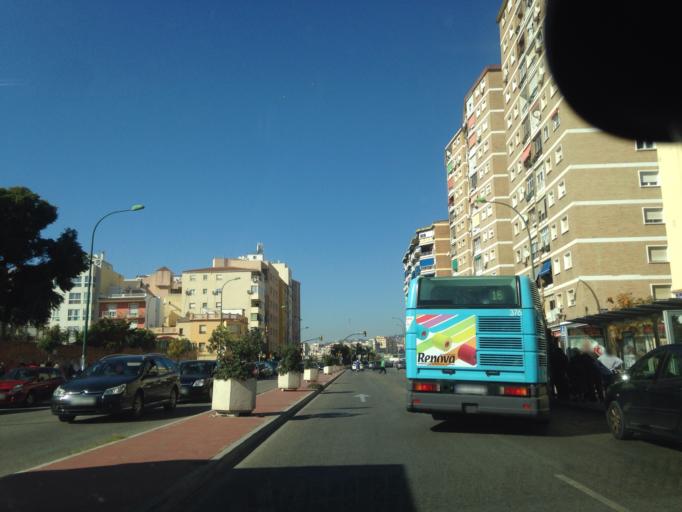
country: ES
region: Andalusia
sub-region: Provincia de Malaga
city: Malaga
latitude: 36.7022
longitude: -4.4392
